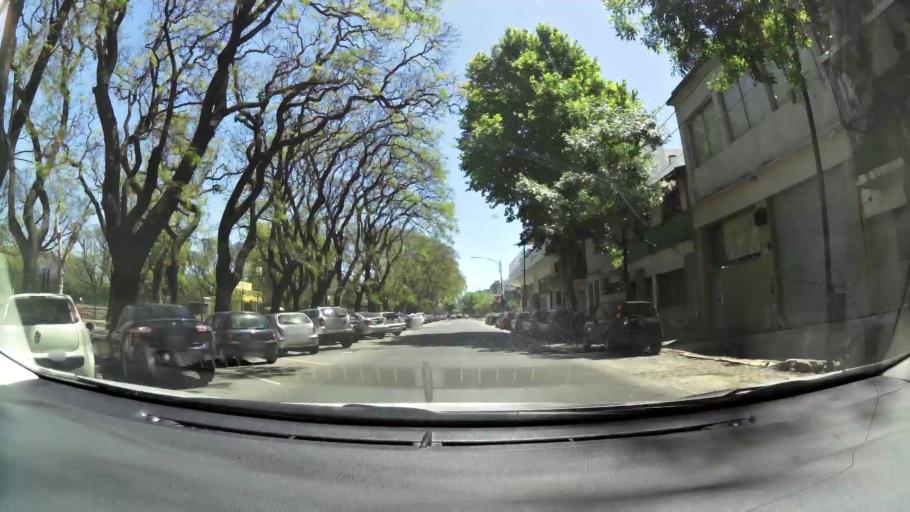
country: AR
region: Buenos Aires F.D.
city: Buenos Aires
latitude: -34.6389
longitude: -58.4053
